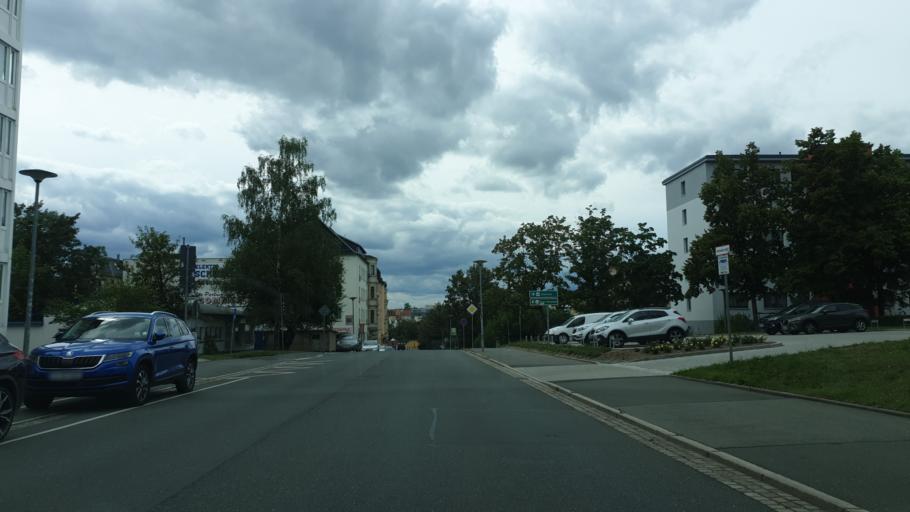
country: DE
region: Saxony
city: Plauen
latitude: 50.5004
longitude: 12.1338
